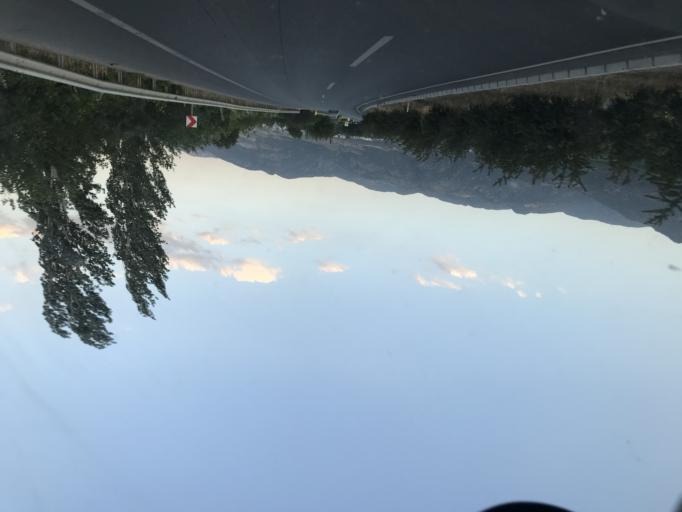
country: TR
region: Aydin
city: Buharkent
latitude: 37.9593
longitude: 28.7195
